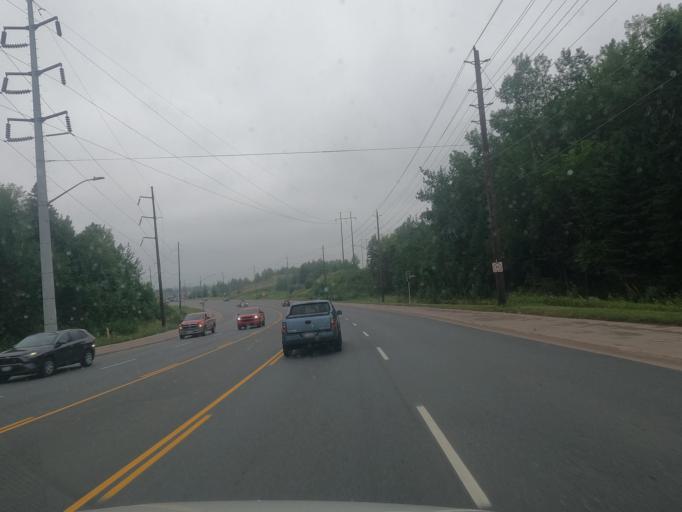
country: CA
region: Ontario
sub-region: Algoma
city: Sault Ste. Marie
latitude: 46.5392
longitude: -84.3416
